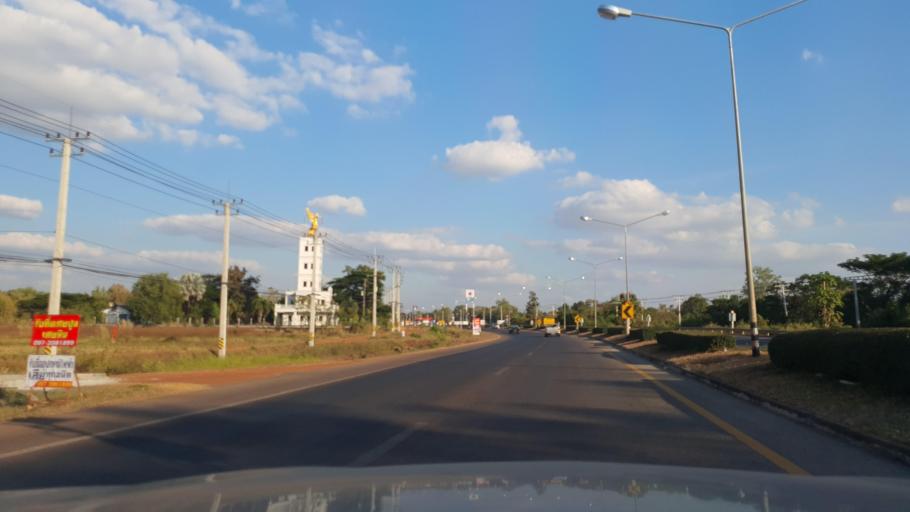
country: TH
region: Sakon Nakhon
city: Sakon Nakhon
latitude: 17.2578
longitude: 104.1621
